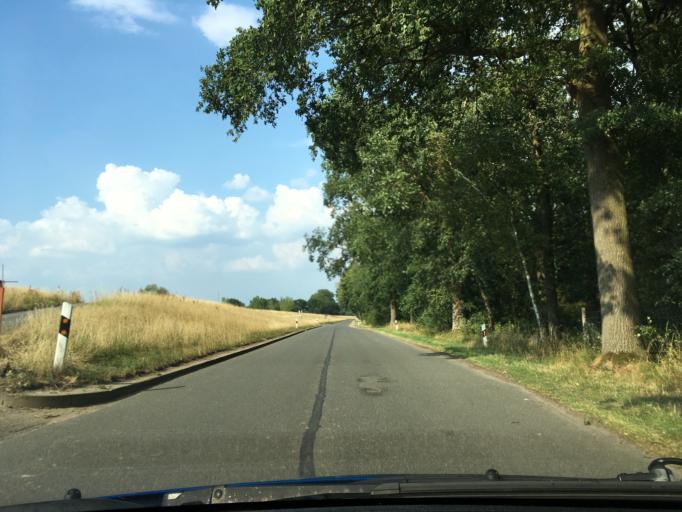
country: DE
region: Lower Saxony
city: Damnatz
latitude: 53.1563
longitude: 11.1285
